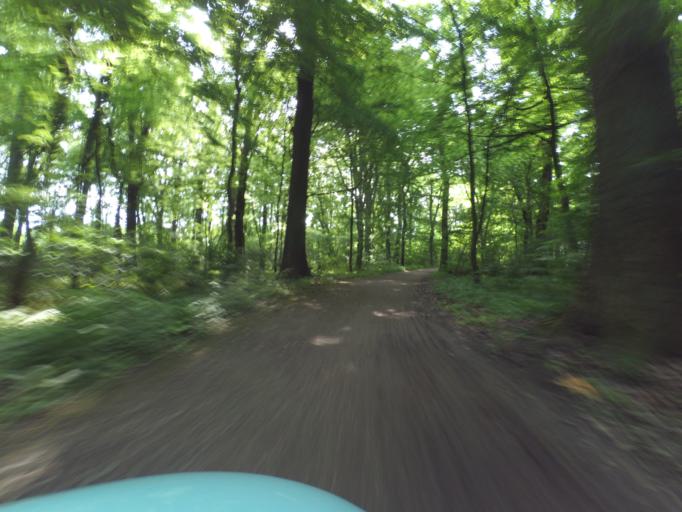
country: DE
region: Lower Saxony
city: Sehnde
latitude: 52.3205
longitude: 9.9593
